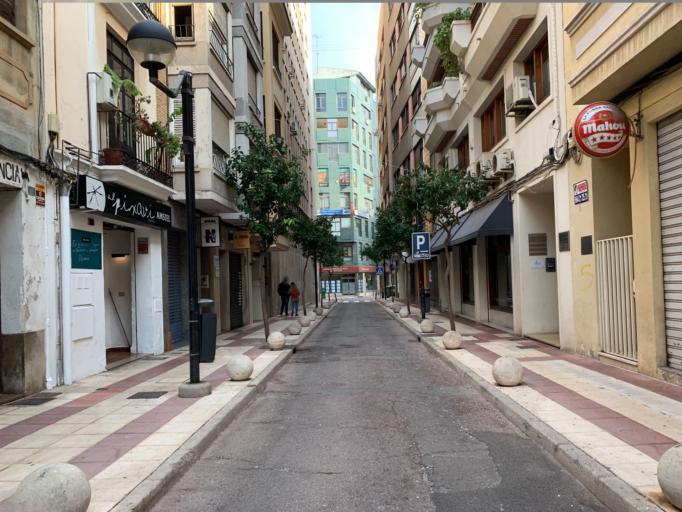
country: ES
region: Valencia
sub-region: Provincia de Castello
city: Castello de la Plana
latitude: 39.9841
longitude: -0.0401
